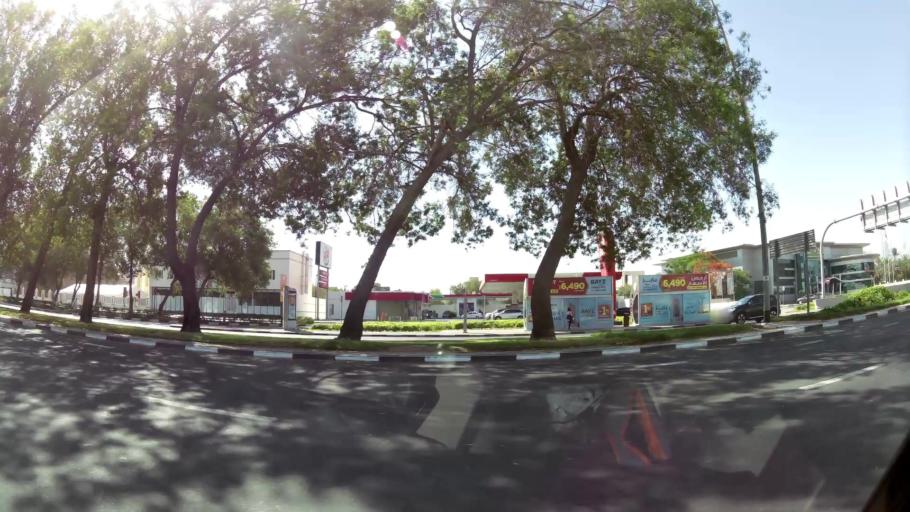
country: AE
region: Ash Shariqah
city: Sharjah
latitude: 25.2502
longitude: 55.2887
